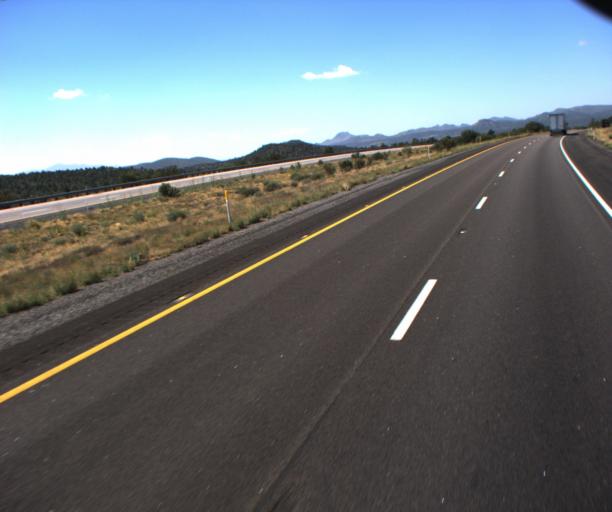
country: US
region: Arizona
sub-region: Mohave County
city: Peach Springs
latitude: 35.1943
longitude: -113.3090
